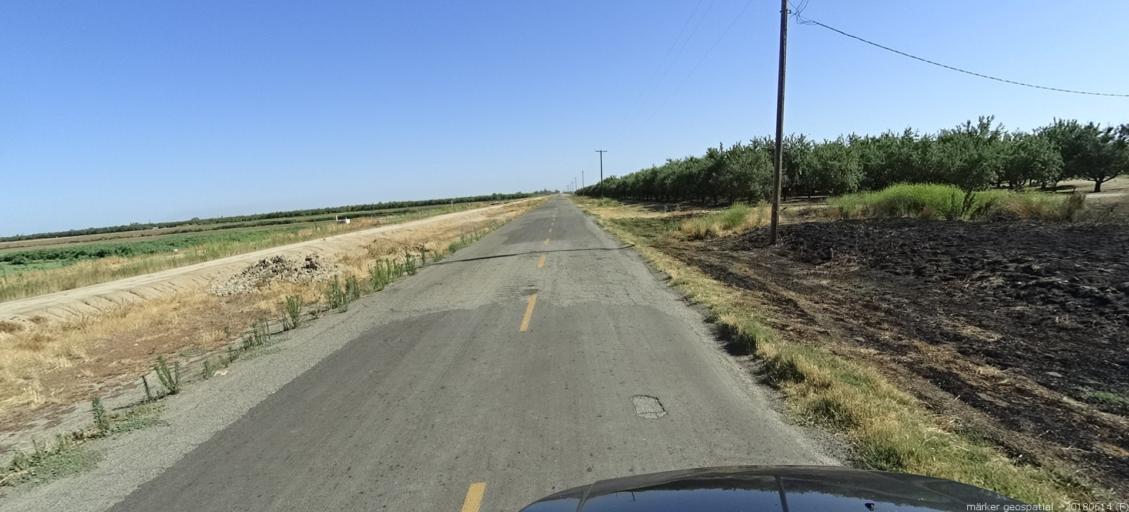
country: US
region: California
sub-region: Madera County
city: Fairmead
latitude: 36.9985
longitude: -120.1661
